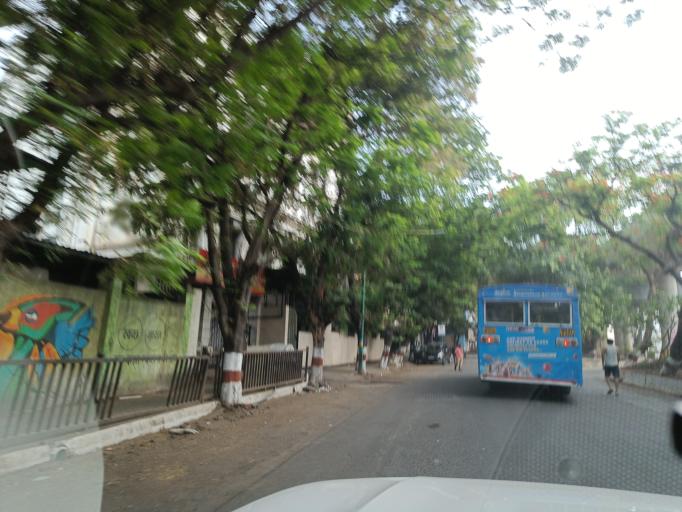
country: IN
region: Maharashtra
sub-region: Thane
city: Thane
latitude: 19.1953
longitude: 72.9622
